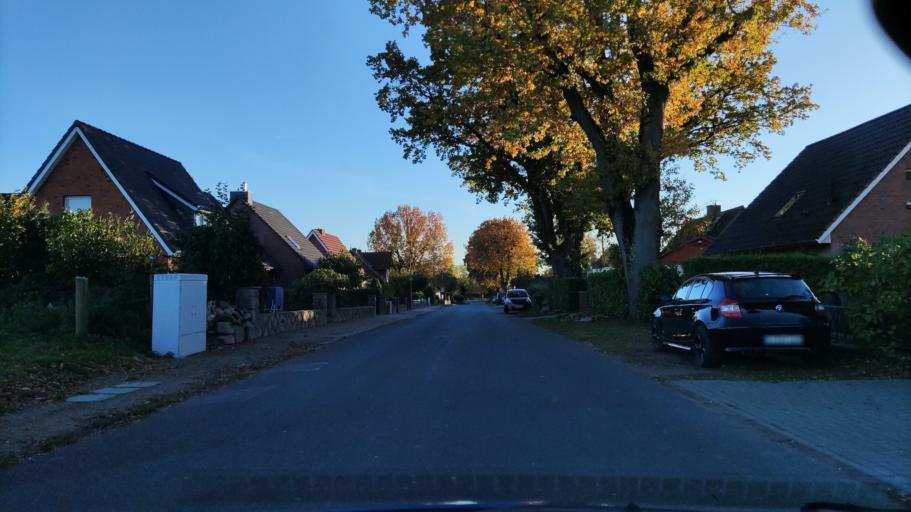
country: DE
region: Schleswig-Holstein
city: Havekost
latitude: 53.5627
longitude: 10.4693
